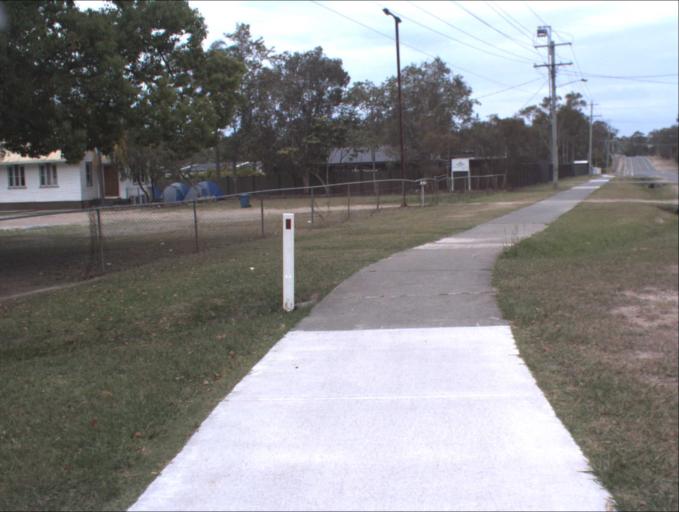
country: AU
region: Queensland
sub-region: Logan
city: Beenleigh
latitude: -27.6651
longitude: 153.2159
